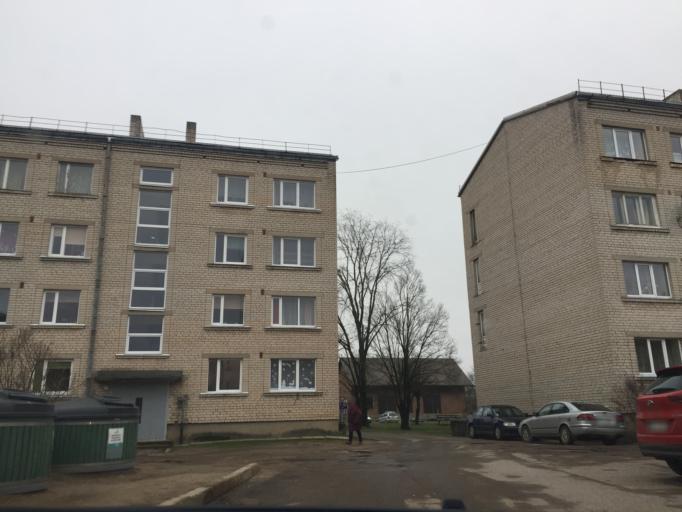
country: LV
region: Limbazu Rajons
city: Limbazi
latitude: 57.5115
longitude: 24.7212
